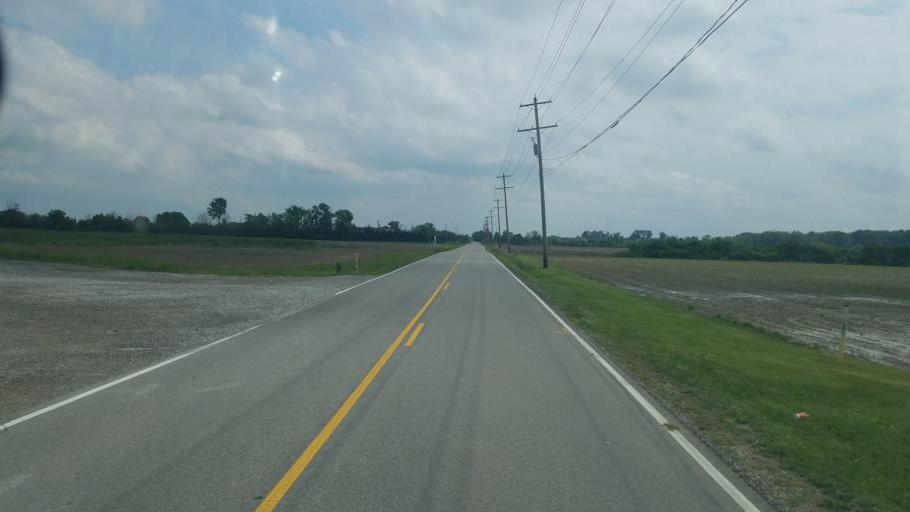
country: US
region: Ohio
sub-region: Franklin County
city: Dublin
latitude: 40.1013
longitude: -83.1756
